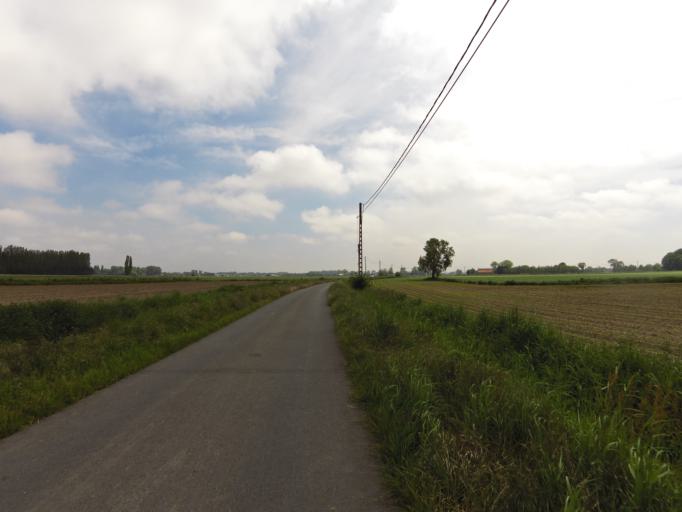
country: BE
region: Flanders
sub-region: Provincie West-Vlaanderen
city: Koekelare
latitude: 51.1247
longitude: 2.9823
